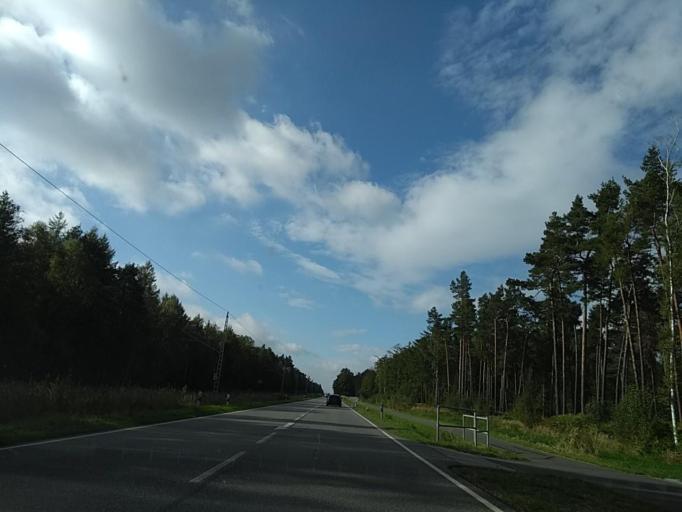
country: DE
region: Mecklenburg-Vorpommern
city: Gelbensande
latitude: 54.1927
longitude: 12.2899
